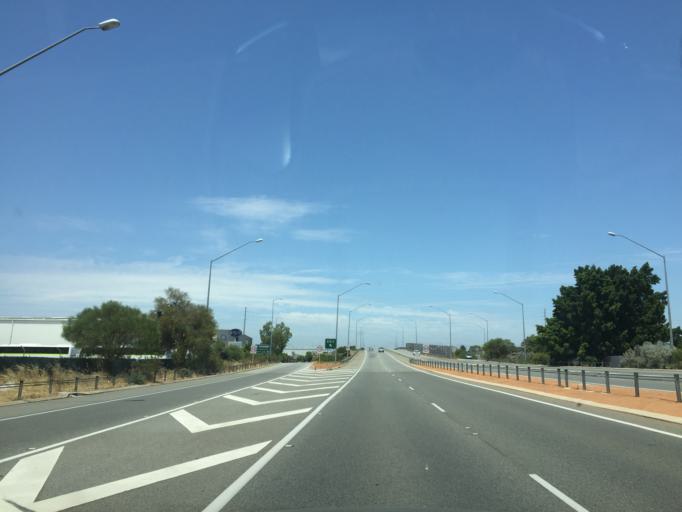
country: AU
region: Western Australia
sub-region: Belmont
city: Kewdale
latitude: -31.9834
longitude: 115.9374
